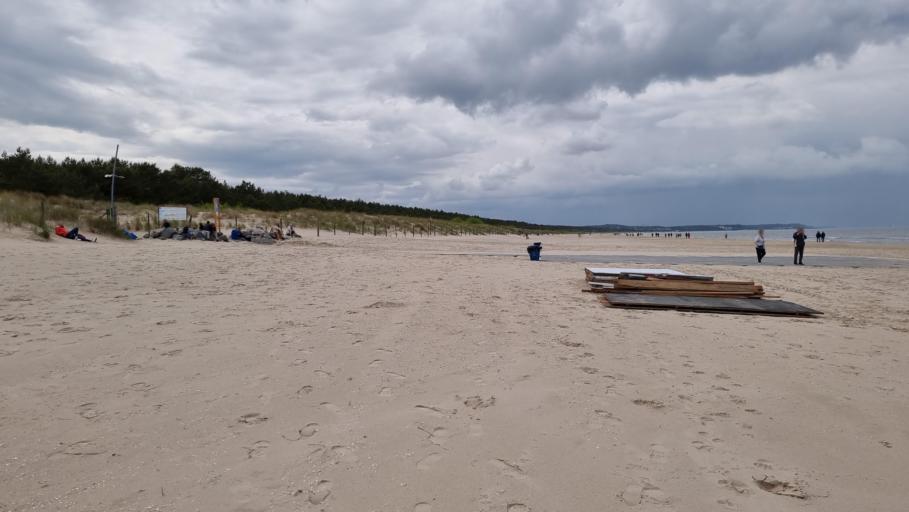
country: PL
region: West Pomeranian Voivodeship
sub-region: Swinoujscie
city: Swinoujscie
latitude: 53.9244
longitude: 14.2414
